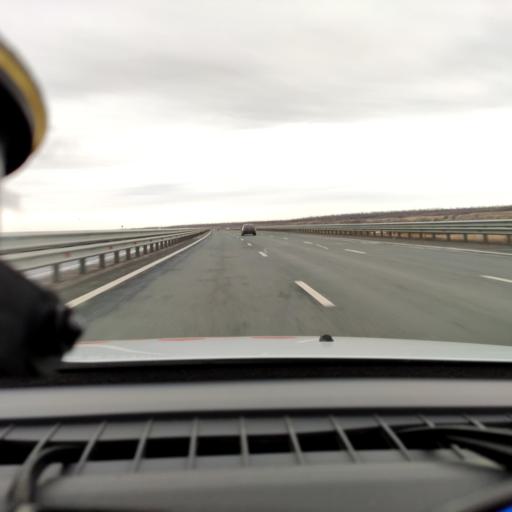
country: RU
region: Samara
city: Smyshlyayevka
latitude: 53.1583
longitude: 50.3337
